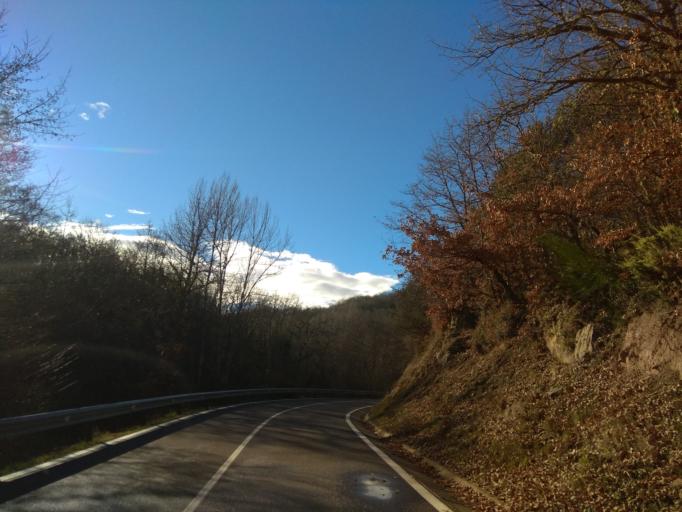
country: ES
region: Cantabria
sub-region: Provincia de Cantabria
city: San Martin de Elines
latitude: 42.9011
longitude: -3.8947
